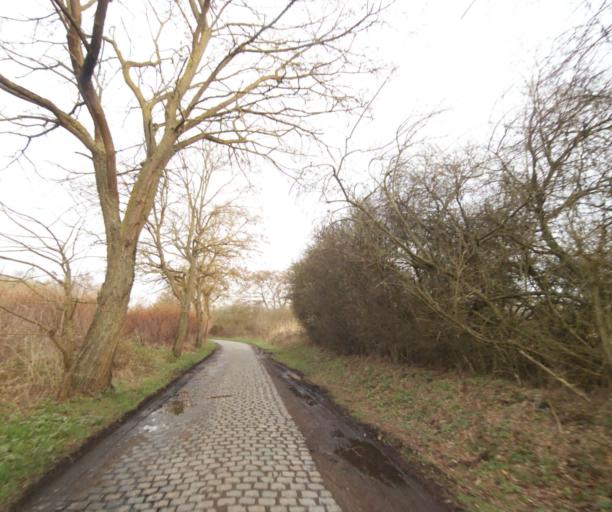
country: BE
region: Wallonia
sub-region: Province du Hainaut
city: Bernissart
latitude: 50.4628
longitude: 3.6233
